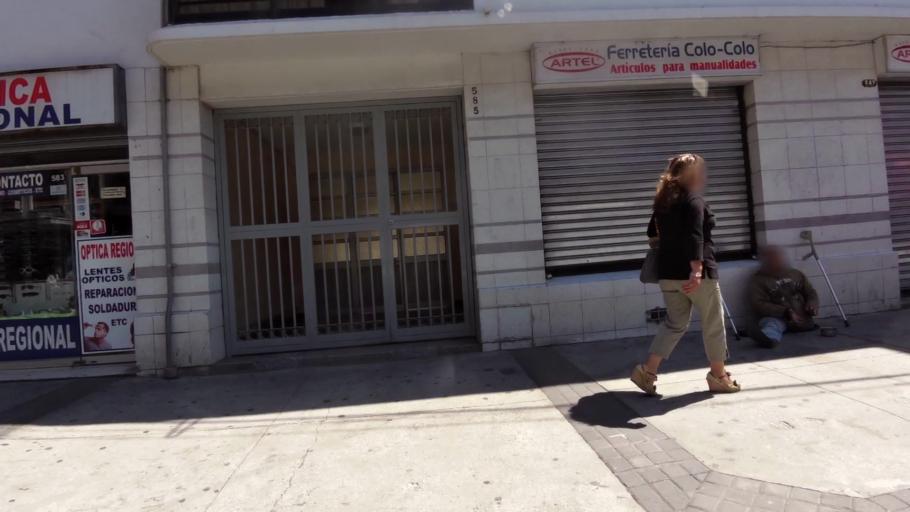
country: CL
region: Biobio
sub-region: Provincia de Concepcion
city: Concepcion
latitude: -36.8250
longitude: -73.0492
